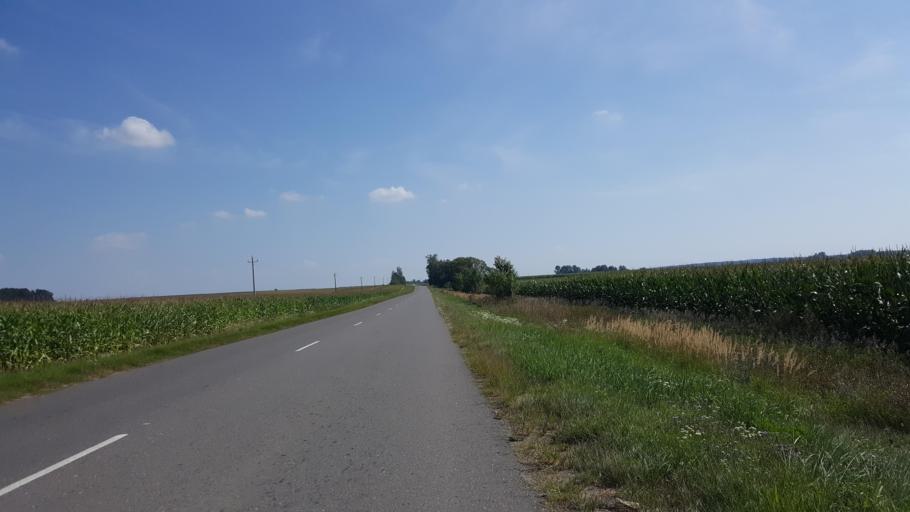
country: BY
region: Brest
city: Kamyanyuki
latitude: 52.4873
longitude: 23.6931
